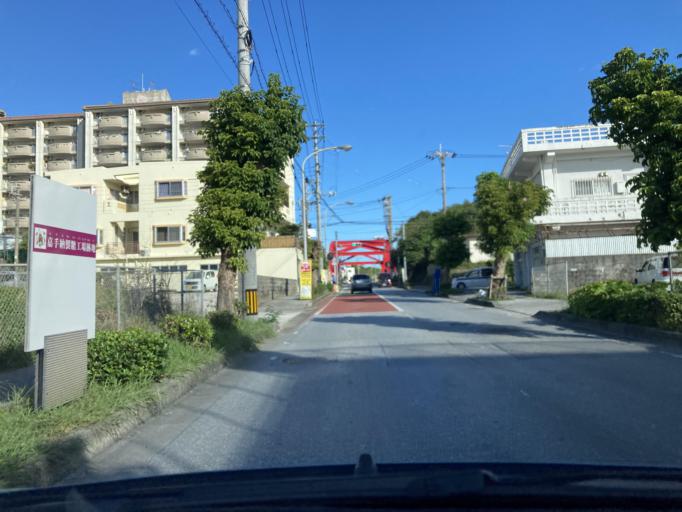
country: JP
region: Okinawa
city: Chatan
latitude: 26.3627
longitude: 127.7484
